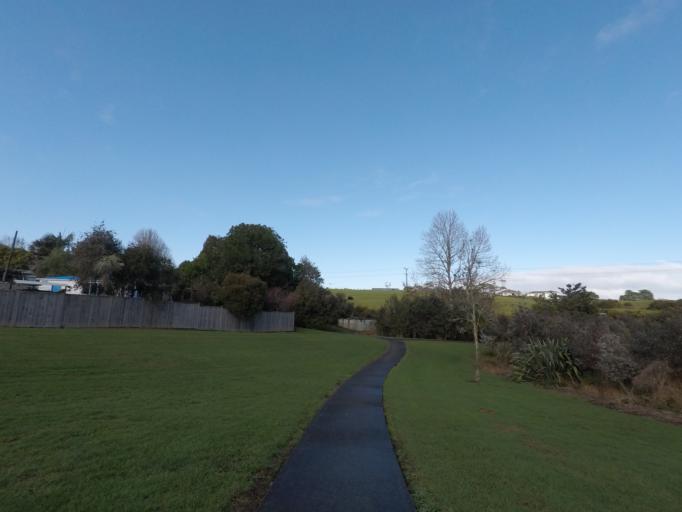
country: NZ
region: Auckland
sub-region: Auckland
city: Warkworth
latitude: -36.4245
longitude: 174.7242
